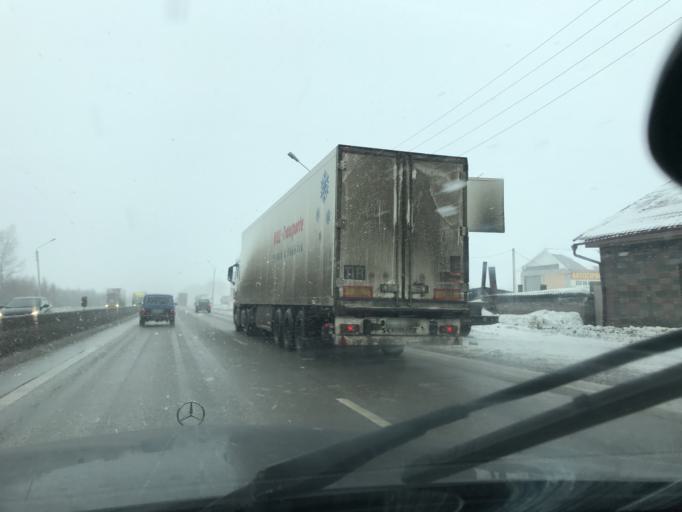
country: RU
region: Nizjnij Novgorod
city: Babino
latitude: 56.3040
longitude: 43.6119
